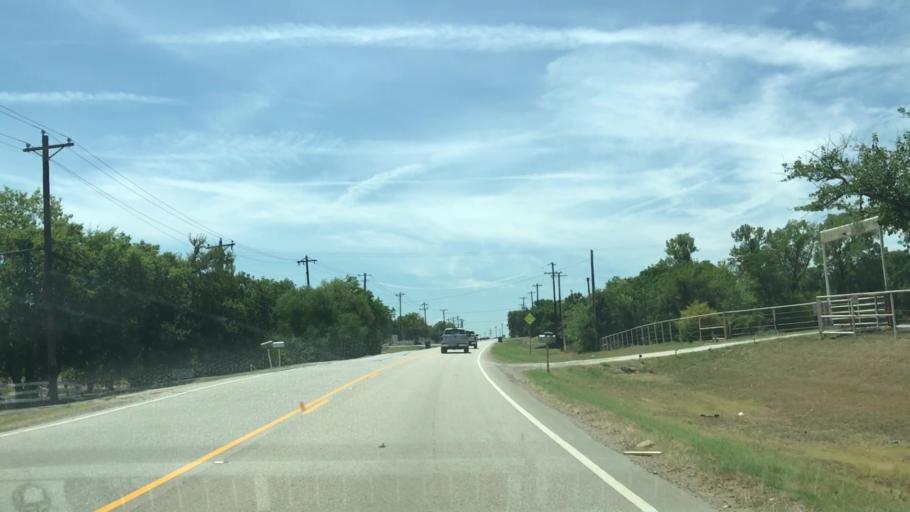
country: US
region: Texas
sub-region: Collin County
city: Saint Paul
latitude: 33.0462
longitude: -96.5496
